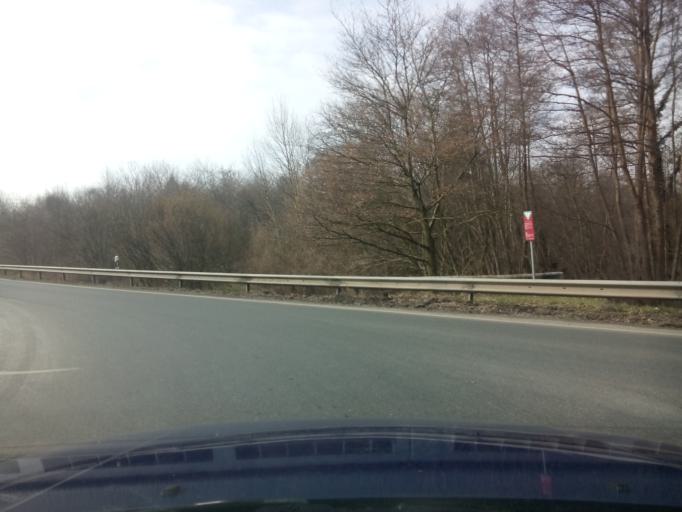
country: DE
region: Lower Saxony
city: Osterholz-Scharmbeck
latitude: 53.2140
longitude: 8.7759
